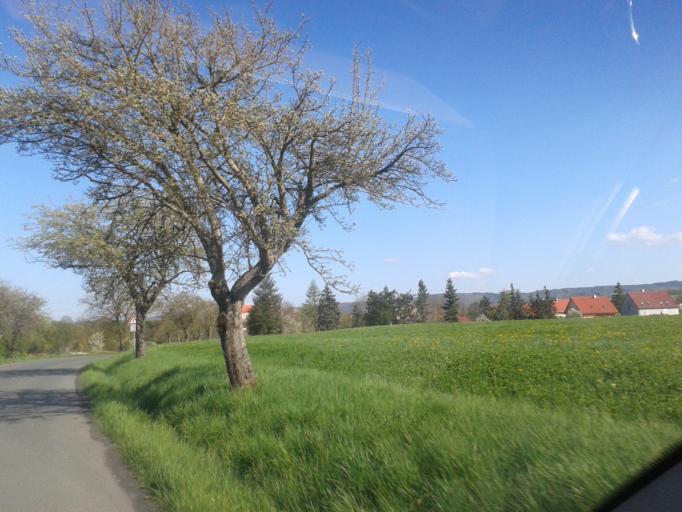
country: CZ
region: Central Bohemia
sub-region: Okres Beroun
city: Lodenice
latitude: 49.9063
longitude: 14.1423
